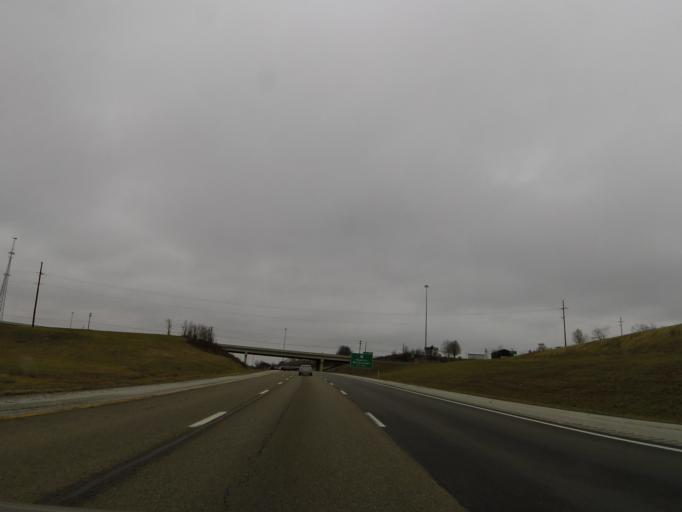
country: US
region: Kentucky
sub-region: Grant County
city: Williamstown
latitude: 38.6488
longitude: -84.5876
